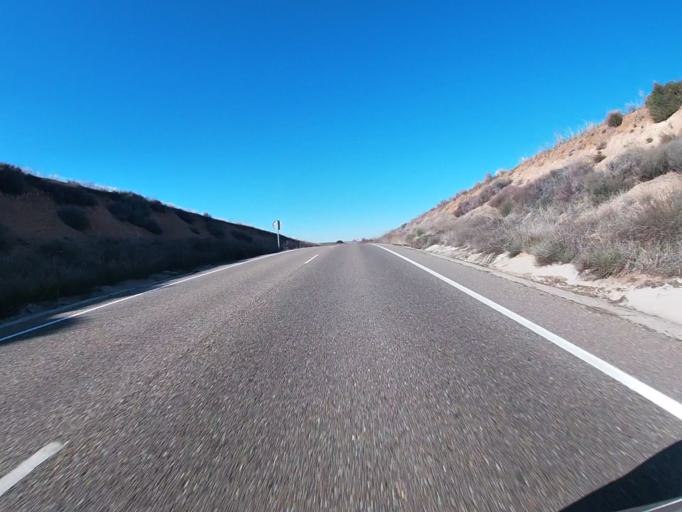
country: ES
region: Castille and Leon
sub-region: Provincia de Salamanca
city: Almenara de Tormes
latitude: 41.0719
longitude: -5.8311
